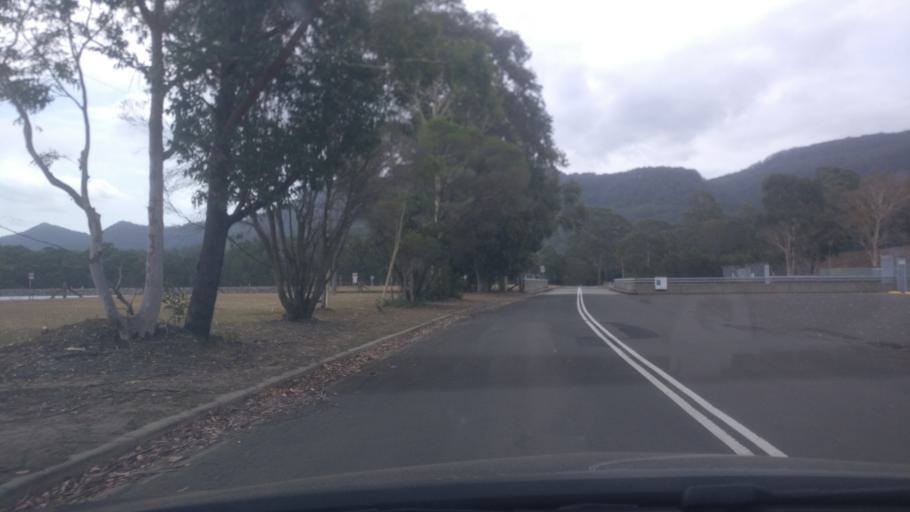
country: AU
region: New South Wales
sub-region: Shoalhaven Shire
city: Kangaroo Valley
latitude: -34.7241
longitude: 150.4797
